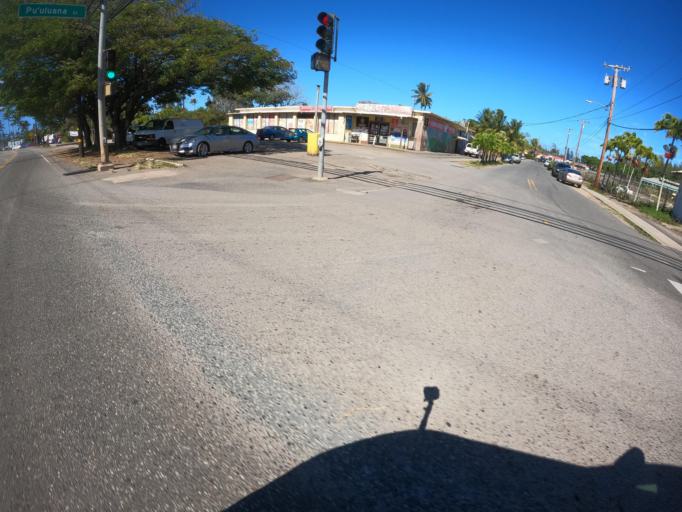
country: US
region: Hawaii
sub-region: Honolulu County
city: Kahuku
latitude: 21.6767
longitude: -157.9474
